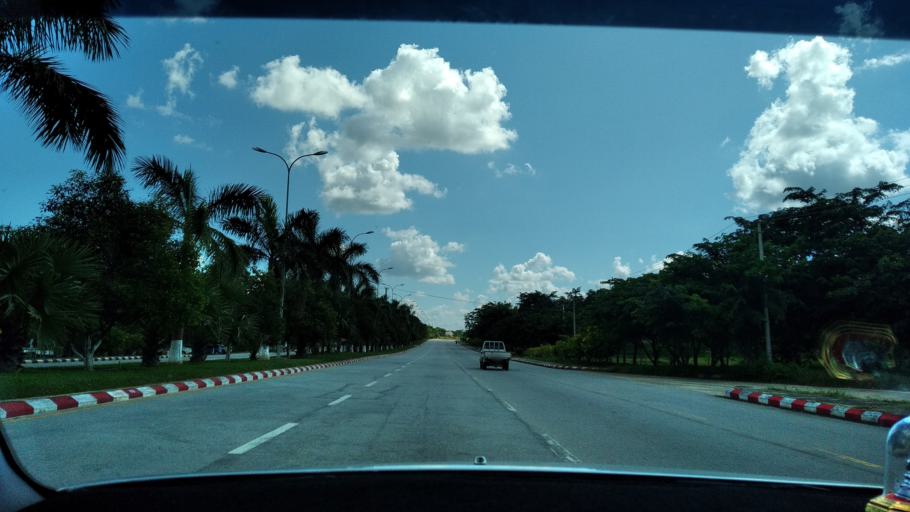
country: MM
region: Mandalay
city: Nay Pyi Taw
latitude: 19.7735
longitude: 96.1427
